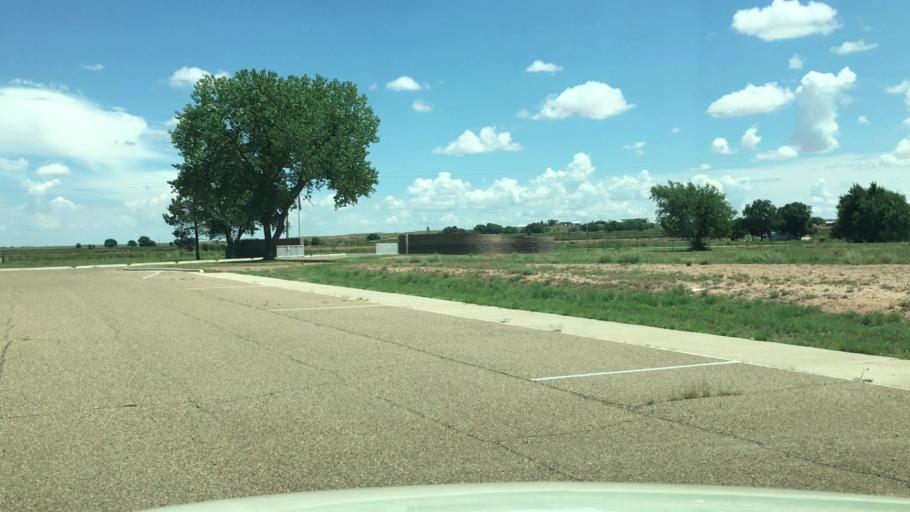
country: US
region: New Mexico
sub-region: De Baca County
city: Fort Sumner
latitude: 34.4014
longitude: -104.1946
